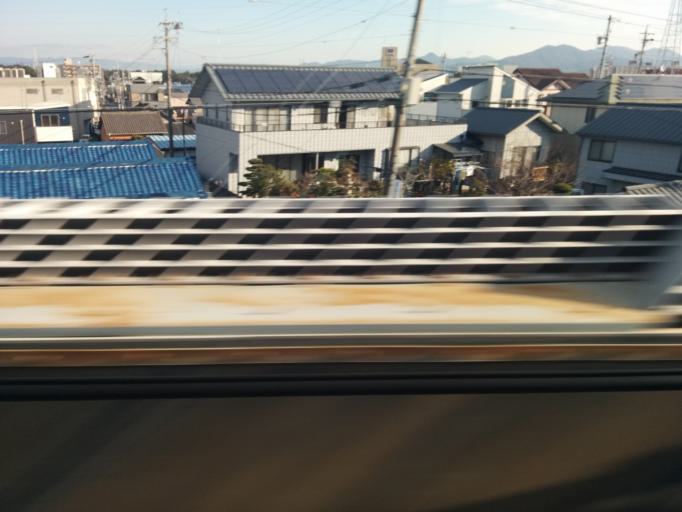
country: JP
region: Aichi
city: Toyohashi
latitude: 34.7458
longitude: 137.3937
